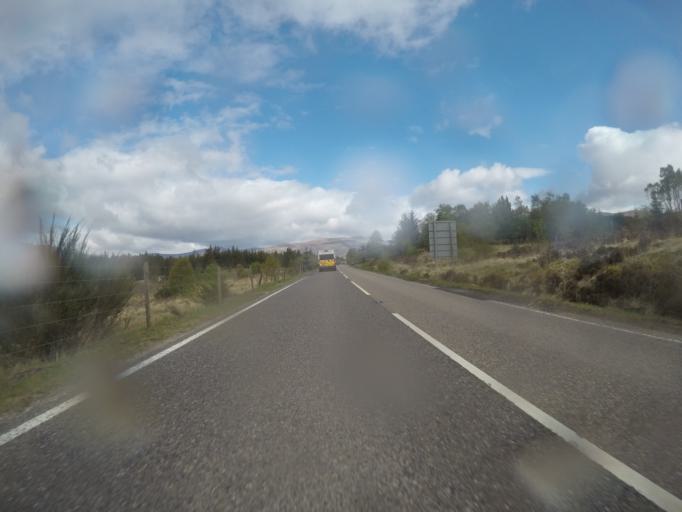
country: GB
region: Scotland
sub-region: Highland
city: Spean Bridge
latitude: 56.9016
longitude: -4.9444
